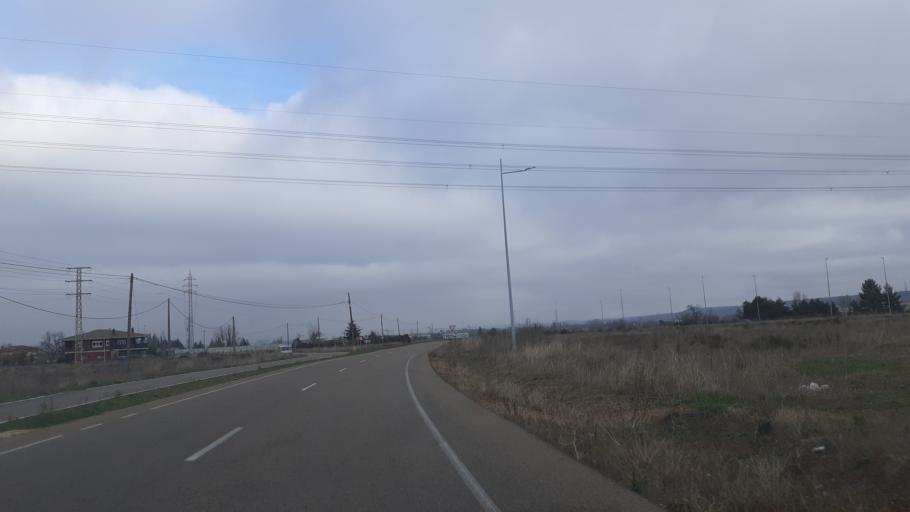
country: ES
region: Castille and Leon
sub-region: Provincia de Leon
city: Onzonilla
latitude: 42.5535
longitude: -5.5845
